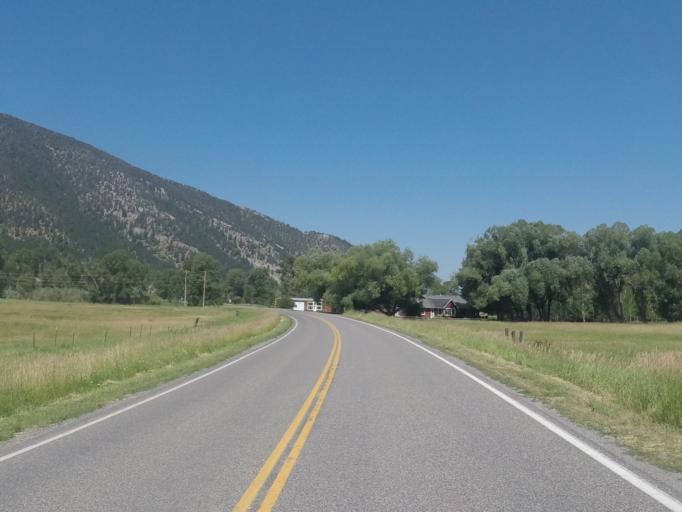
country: US
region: Montana
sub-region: Park County
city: Livingston
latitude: 45.5955
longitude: -110.5627
